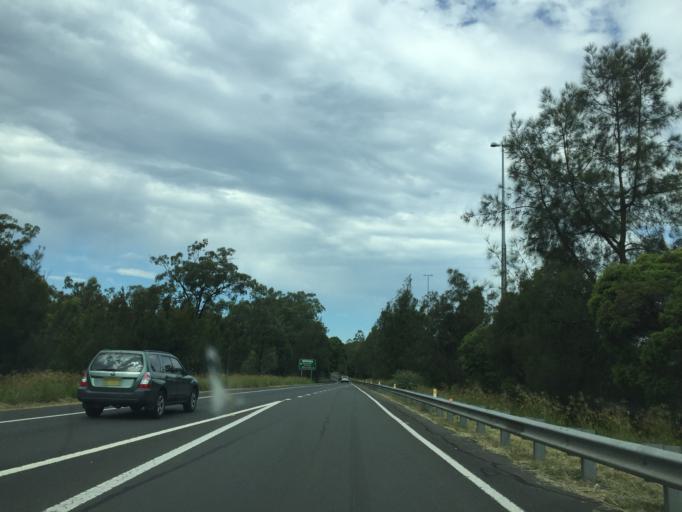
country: AU
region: New South Wales
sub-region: Blacktown
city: Doonside
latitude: -33.8022
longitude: 150.8915
